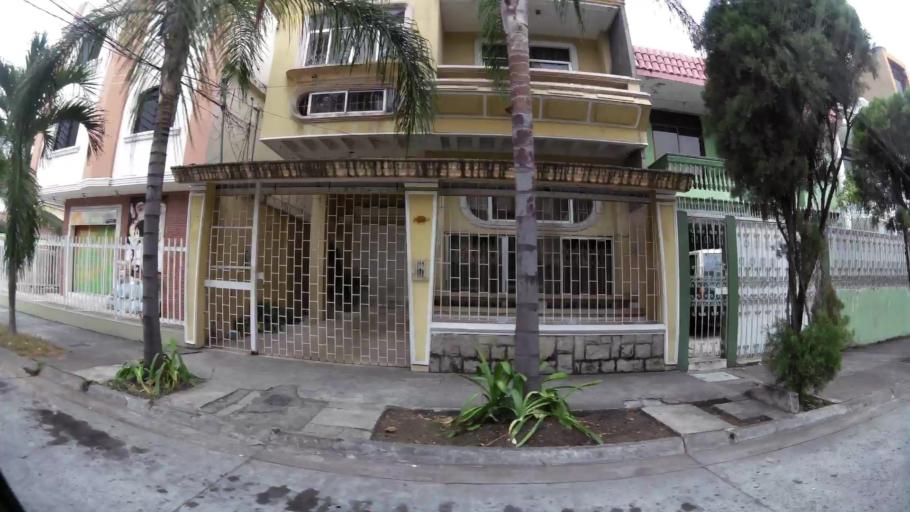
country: EC
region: Guayas
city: Eloy Alfaro
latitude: -2.1449
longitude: -79.8909
